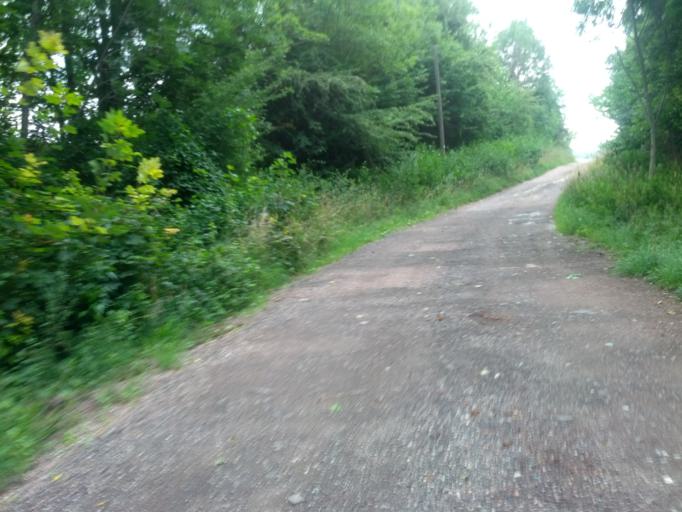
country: DE
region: Thuringia
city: Eisenach
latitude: 50.9927
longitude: 10.3713
